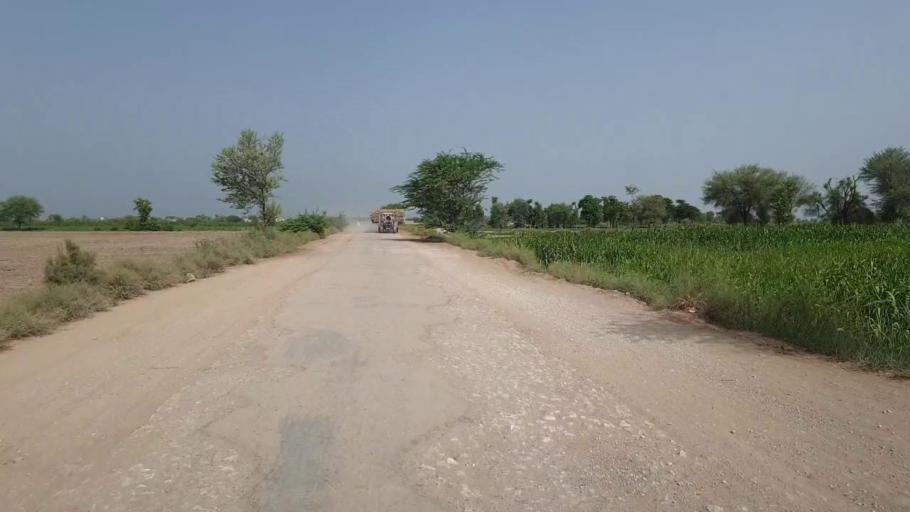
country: PK
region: Sindh
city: Daulatpur
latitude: 26.5497
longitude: 68.0585
